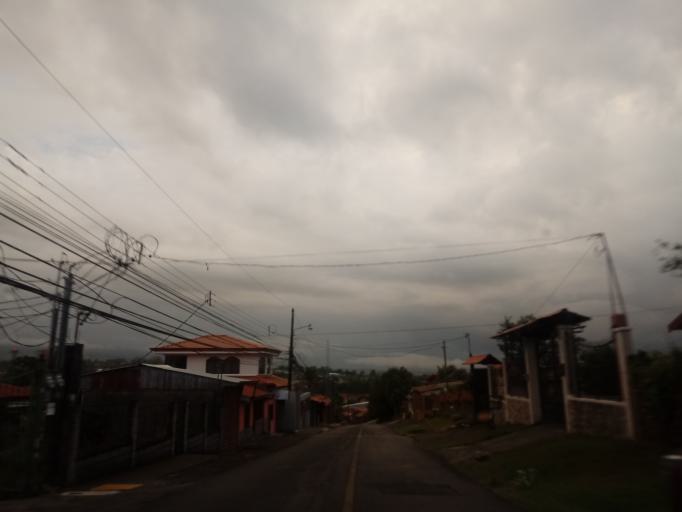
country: CR
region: Heredia
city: Angeles
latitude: 10.0222
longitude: -84.0388
